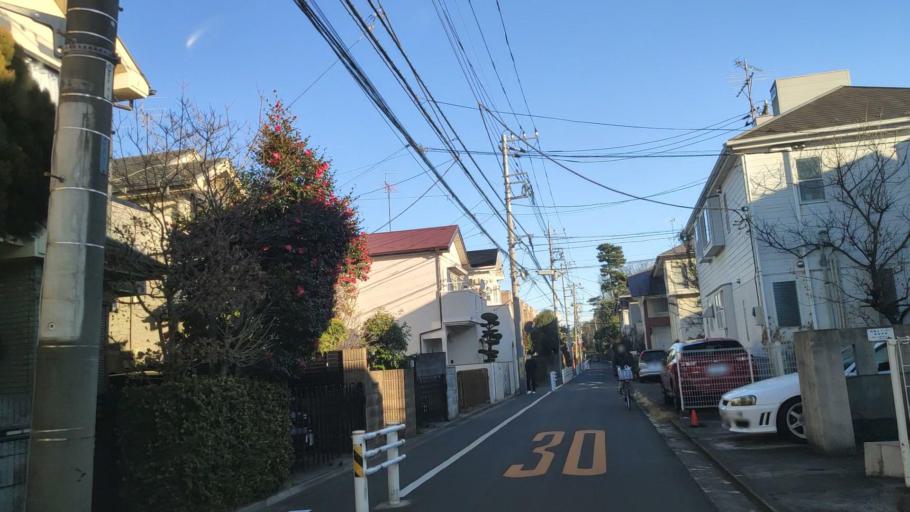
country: JP
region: Tokyo
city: Musashino
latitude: 35.7028
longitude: 139.5693
